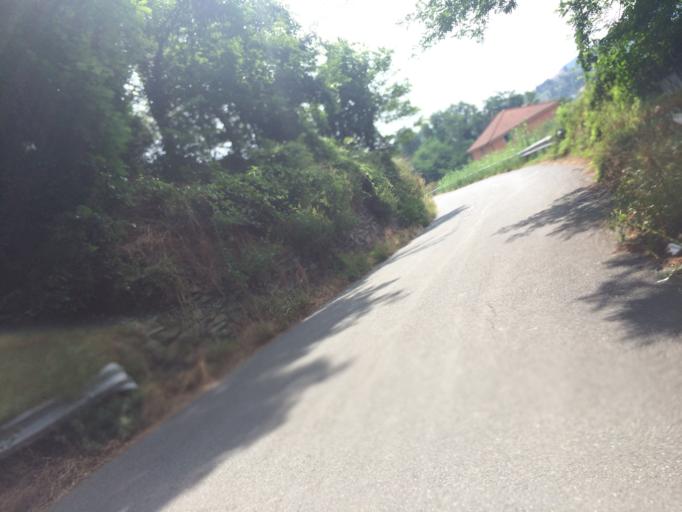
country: IT
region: Liguria
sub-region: Provincia di Savona
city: San Giovanni
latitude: 44.3922
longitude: 8.5188
